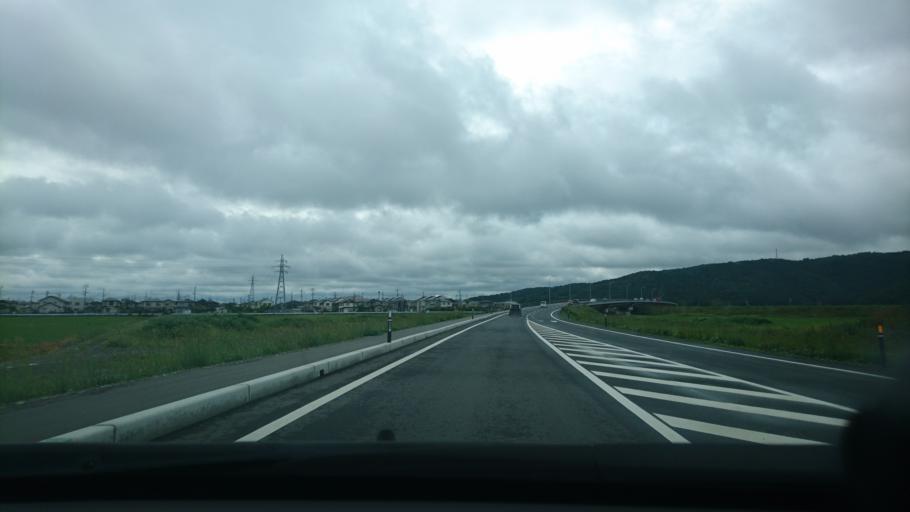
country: JP
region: Miyagi
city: Ishinomaki
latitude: 38.4493
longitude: 141.3417
